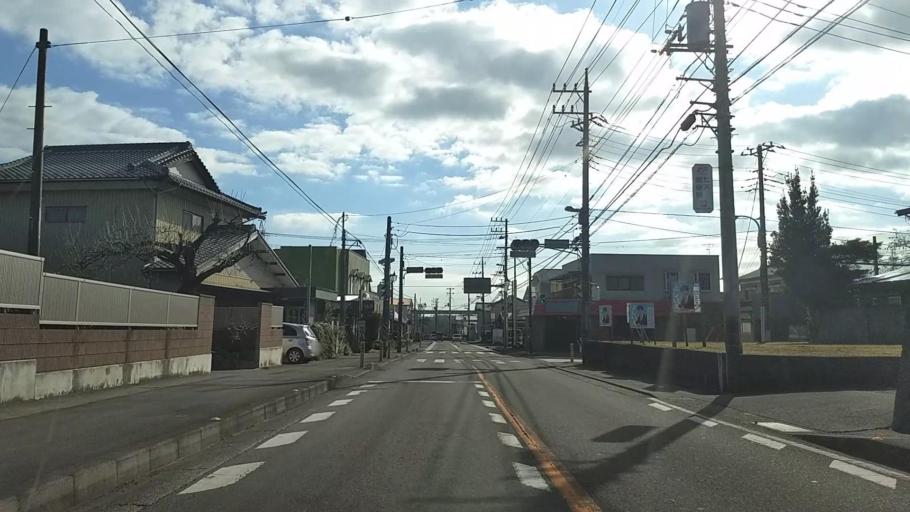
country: JP
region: Kanagawa
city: Isehara
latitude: 35.4428
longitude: 139.2990
